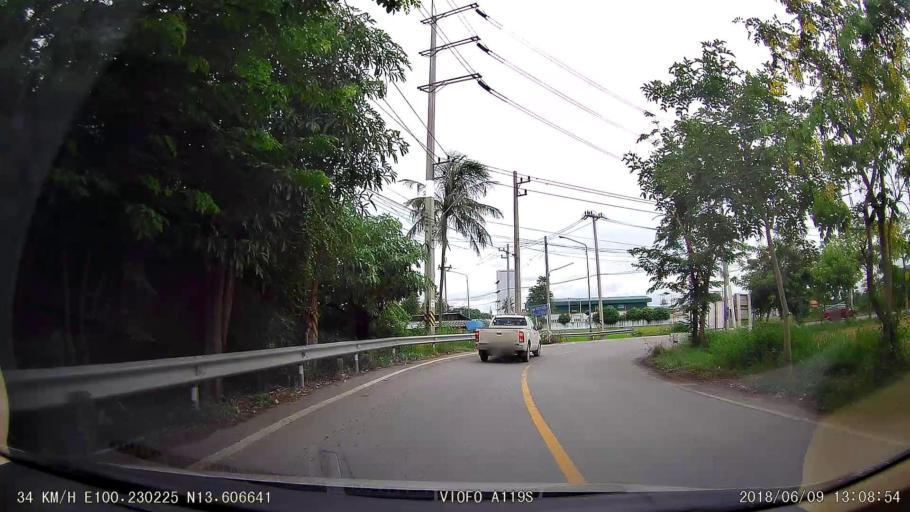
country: TH
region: Samut Sakhon
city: Krathum Baen
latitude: 13.6063
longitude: 100.2308
